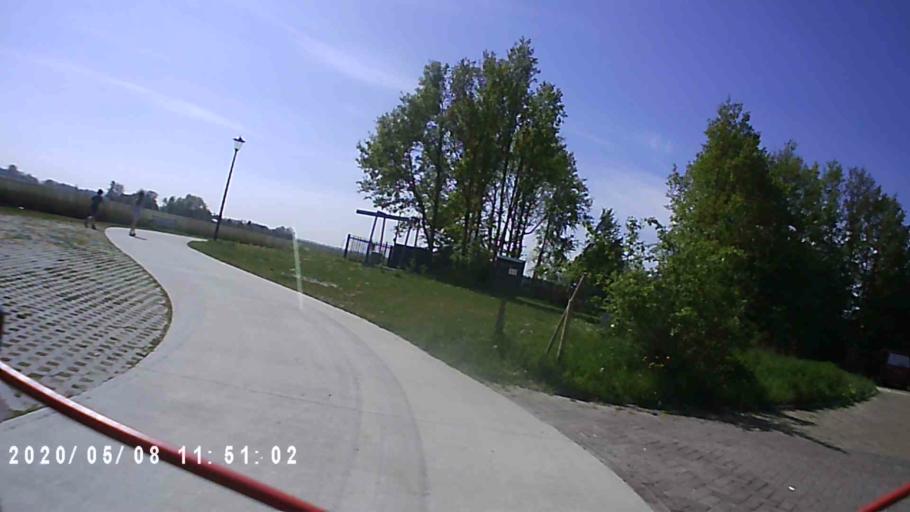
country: NL
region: Groningen
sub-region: Gemeente Bedum
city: Bedum
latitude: 53.3199
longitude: 6.6945
